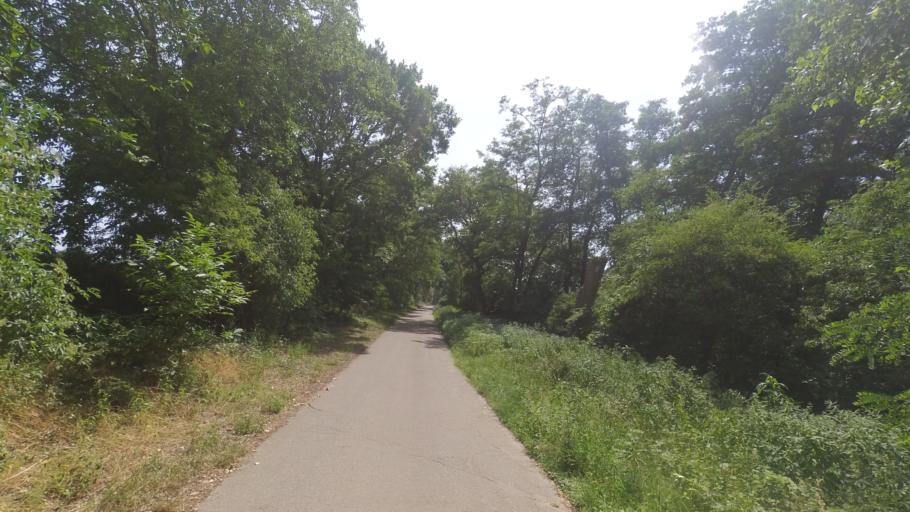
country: DE
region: Rheinland-Pfalz
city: Waldsee
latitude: 49.4071
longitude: 8.4287
